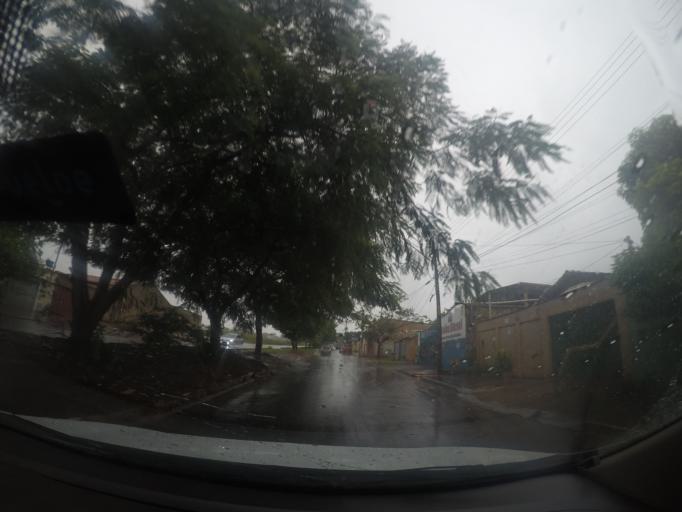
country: BR
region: Goias
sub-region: Goiania
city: Goiania
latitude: -16.5951
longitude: -49.3251
